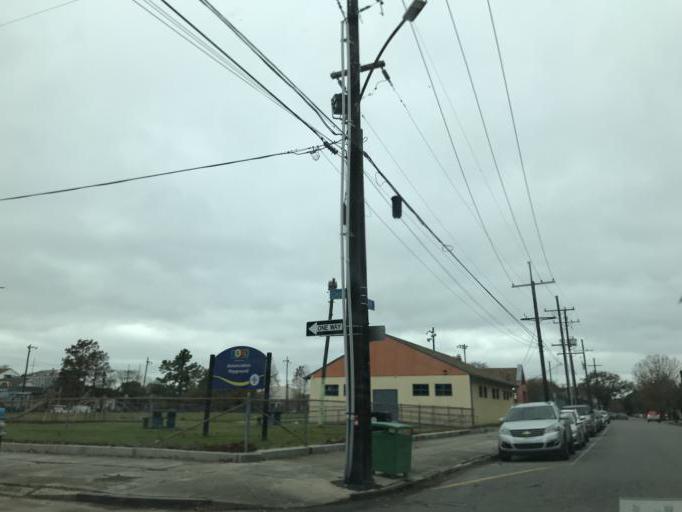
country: US
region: Louisiana
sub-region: Orleans Parish
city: New Orleans
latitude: 29.9336
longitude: -90.0687
